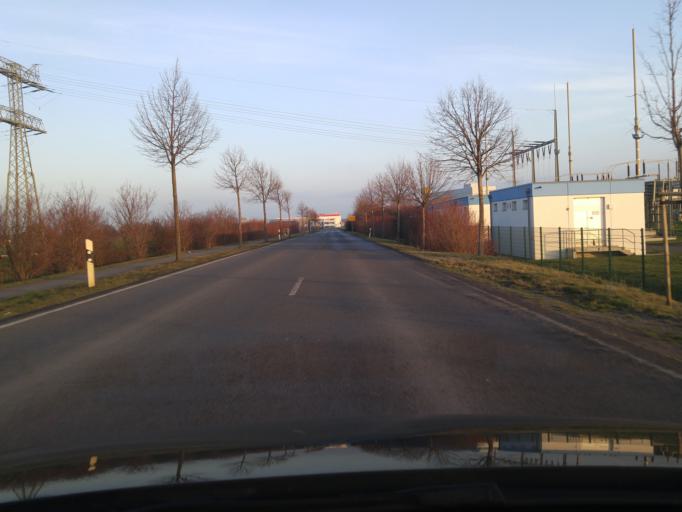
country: DE
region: Saxony
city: Zwochau
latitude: 51.4142
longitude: 12.2849
